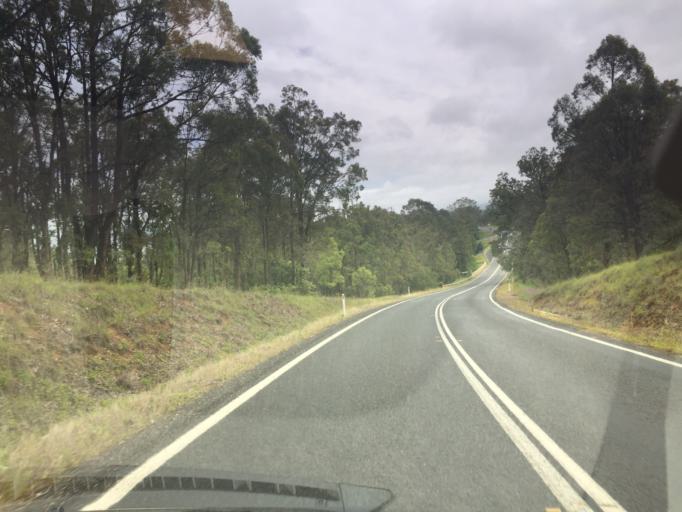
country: AU
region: New South Wales
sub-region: Bega Valley
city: Bega
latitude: -36.6375
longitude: 149.5775
